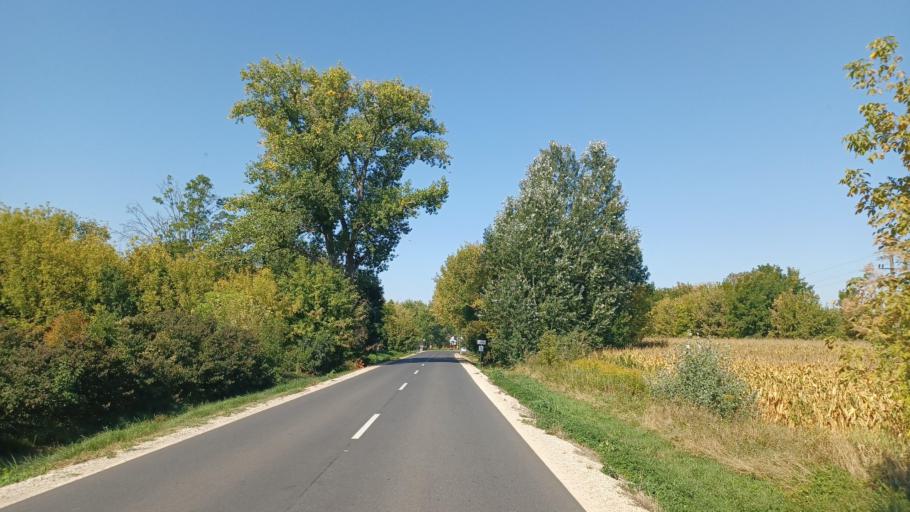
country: HU
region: Fejer
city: Cece
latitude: 46.7630
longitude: 18.6443
